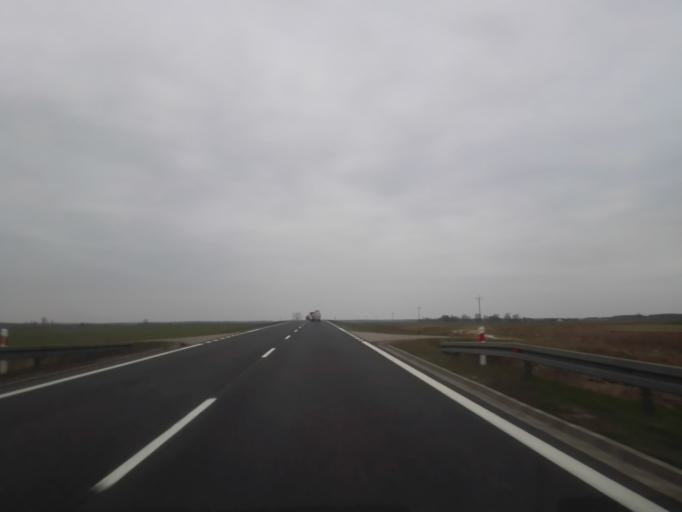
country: PL
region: Podlasie
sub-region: Powiat kolnenski
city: Stawiski
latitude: 53.4121
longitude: 22.1623
